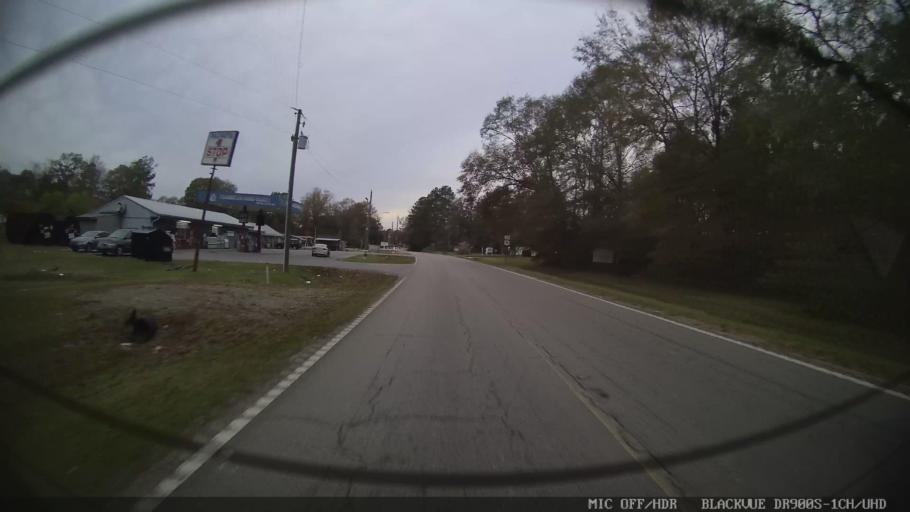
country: US
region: Mississippi
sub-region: Clarke County
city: Stonewall
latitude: 32.0391
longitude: -88.8807
